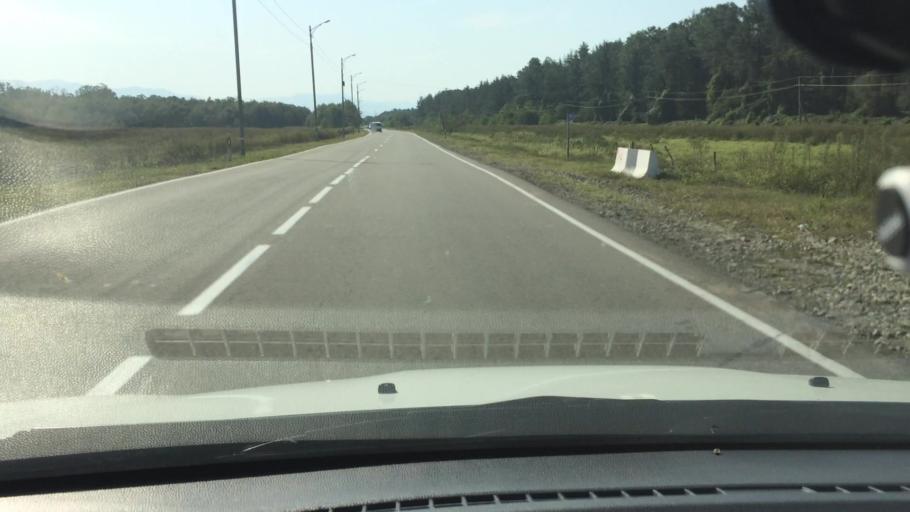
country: GE
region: Guria
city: Urek'i
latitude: 41.9498
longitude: 41.7701
